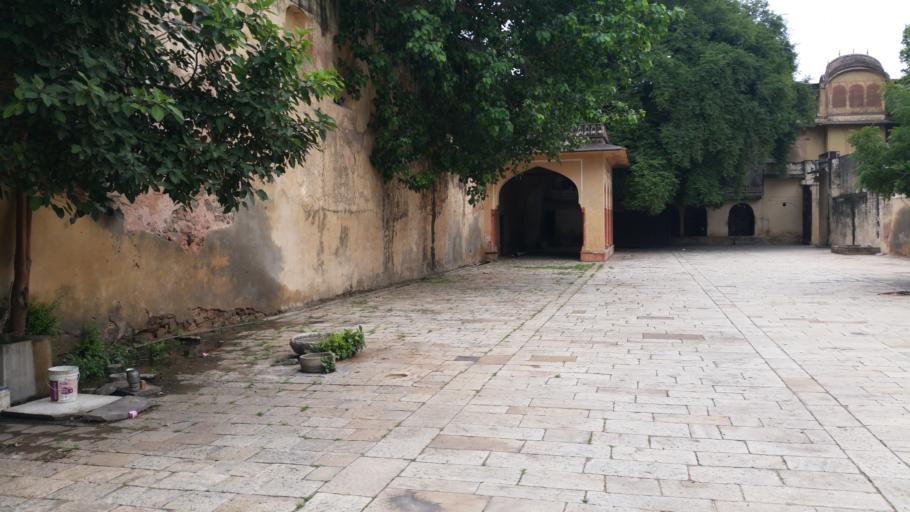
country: IN
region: Rajasthan
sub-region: Jaipur
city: Jaipur
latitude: 26.9255
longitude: 75.8220
